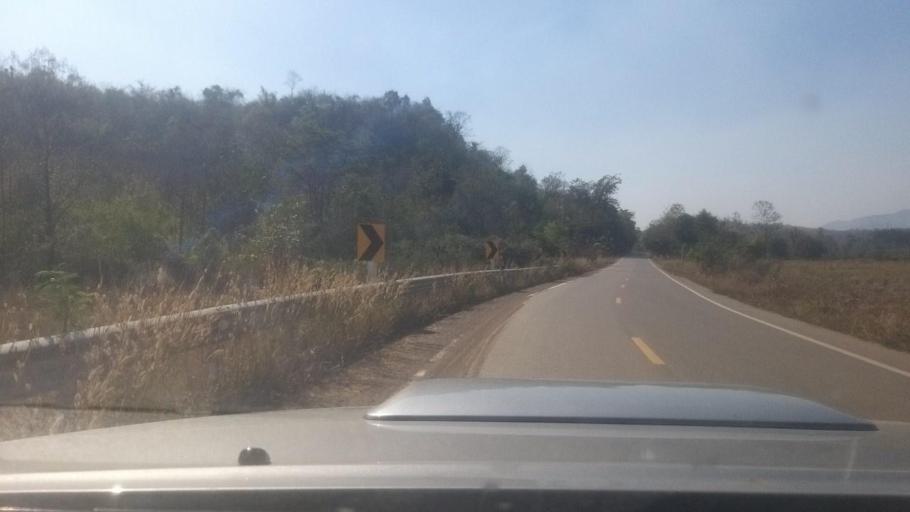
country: TH
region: Phrae
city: Nong Muang Khai
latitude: 18.2946
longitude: 100.0366
